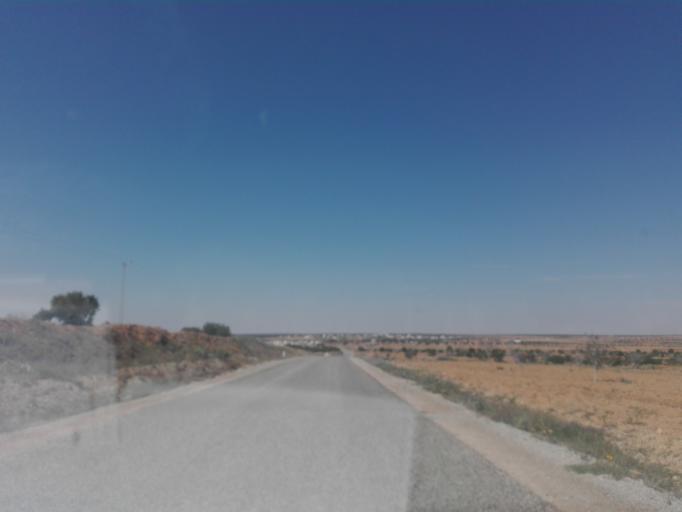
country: TN
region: Safaqis
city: Bi'r `Ali Bin Khalifah
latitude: 34.6735
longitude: 10.3787
